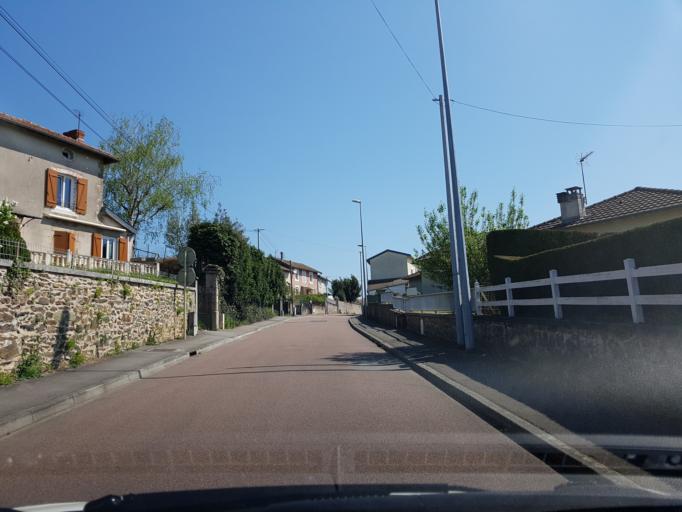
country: FR
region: Limousin
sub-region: Departement de la Haute-Vienne
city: Saint-Junien
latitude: 45.8880
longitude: 0.9100
